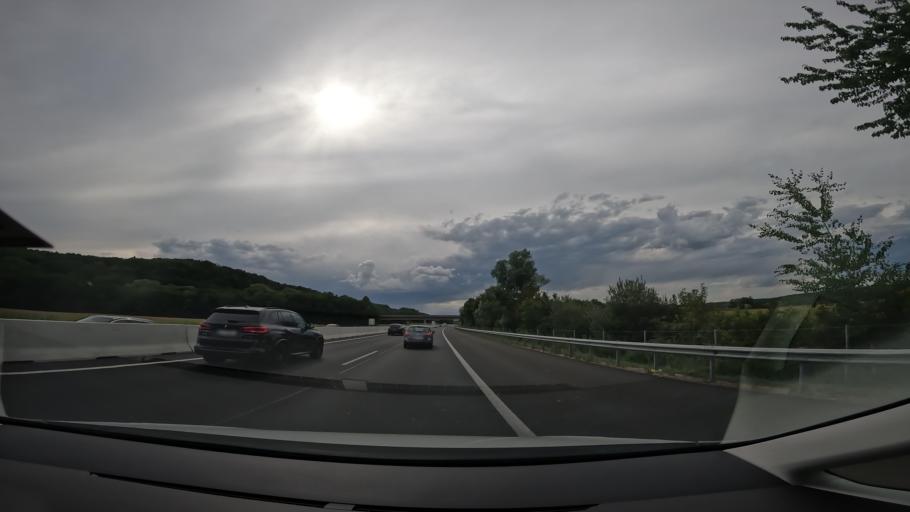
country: AT
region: Styria
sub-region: Politischer Bezirk Hartberg-Fuerstenfeld
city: Ilz
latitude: 47.0777
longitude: 15.9473
